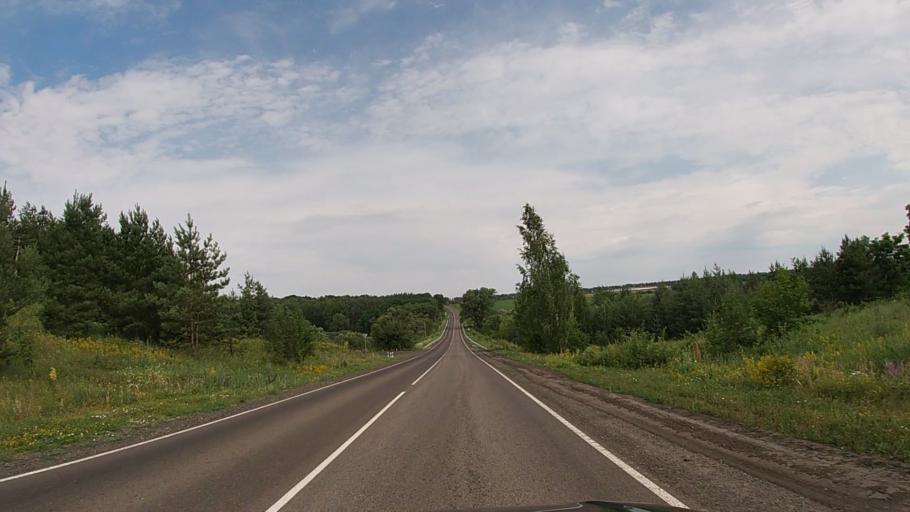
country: RU
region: Belgorod
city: Krasnaya Yaruga
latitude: 50.8258
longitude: 35.4984
